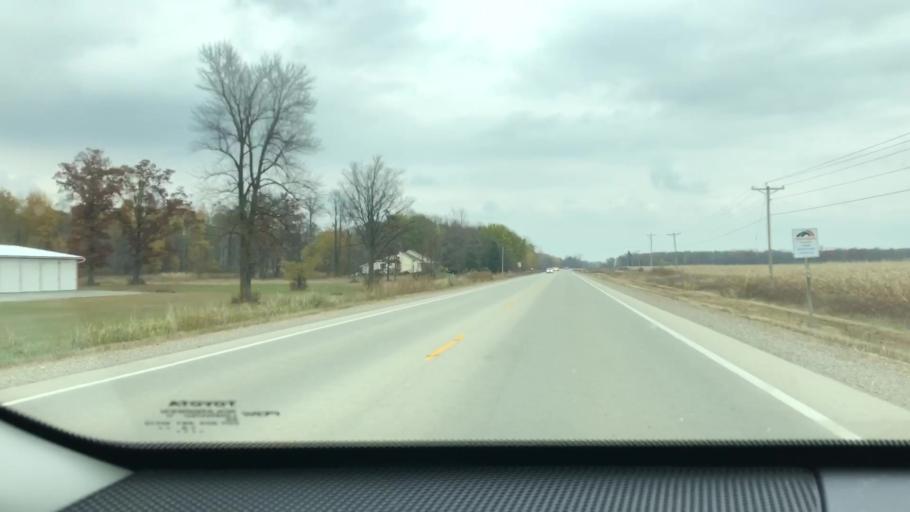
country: US
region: Wisconsin
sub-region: Brown County
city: Oneida
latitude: 44.5025
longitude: -88.2487
